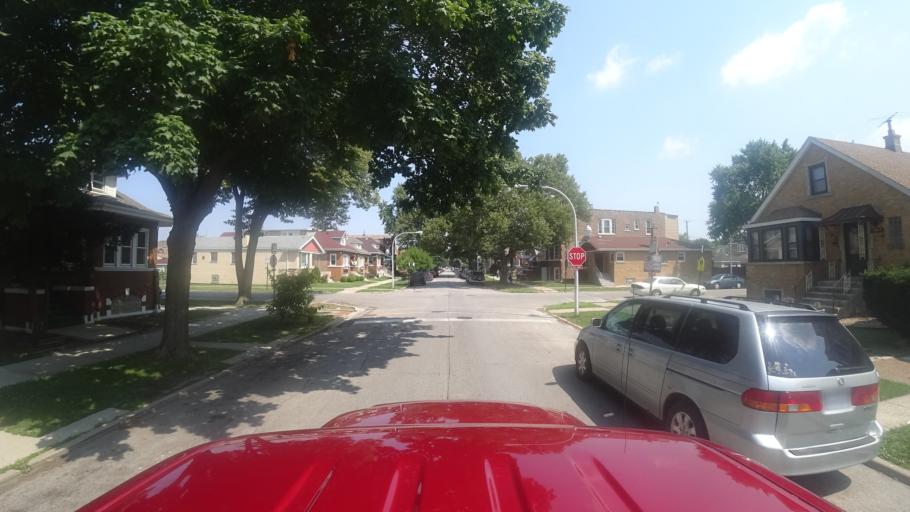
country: US
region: Illinois
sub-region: Cook County
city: Cicero
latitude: 41.8039
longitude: -87.7272
